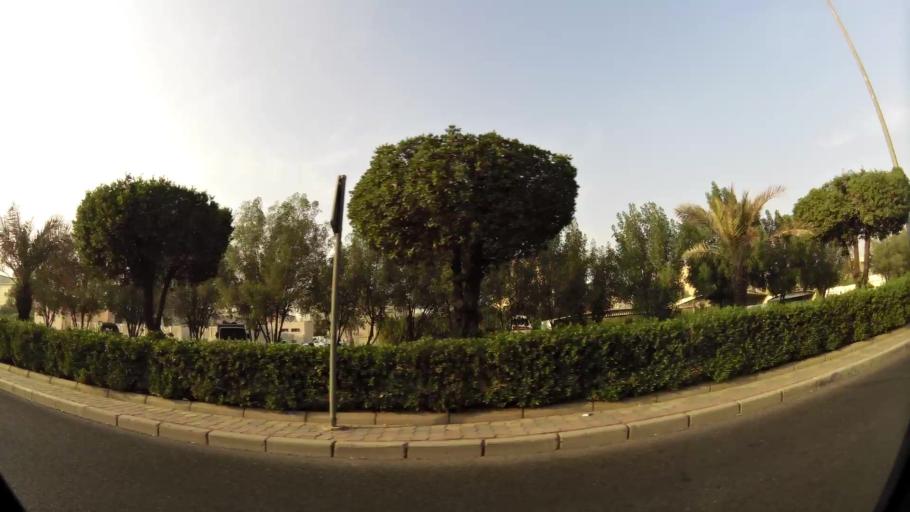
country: KW
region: Mubarak al Kabir
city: Sabah as Salim
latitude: 29.2409
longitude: 48.0587
